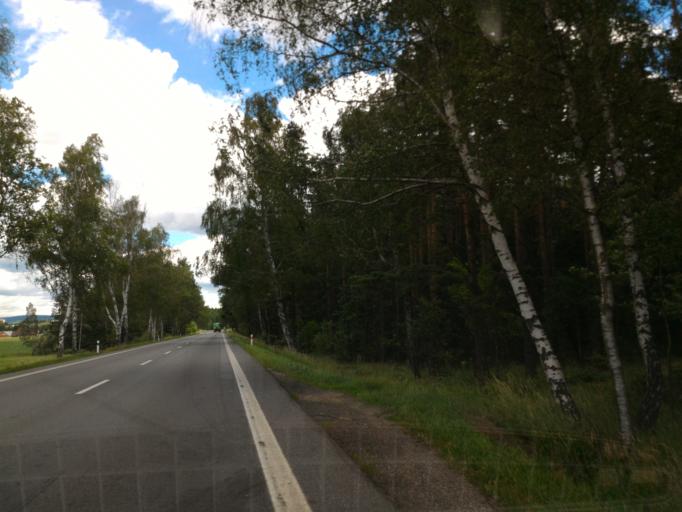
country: CZ
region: Vysocina
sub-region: Okres Zd'ar nad Sazavou
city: Zd'ar nad Sazavou
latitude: 49.5412
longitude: 15.9287
